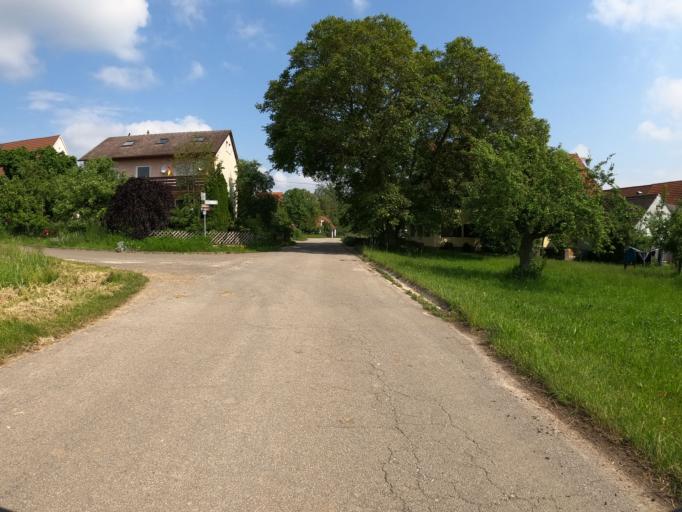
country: DE
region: Bavaria
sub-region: Swabia
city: Holzheim
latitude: 48.3601
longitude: 10.0992
